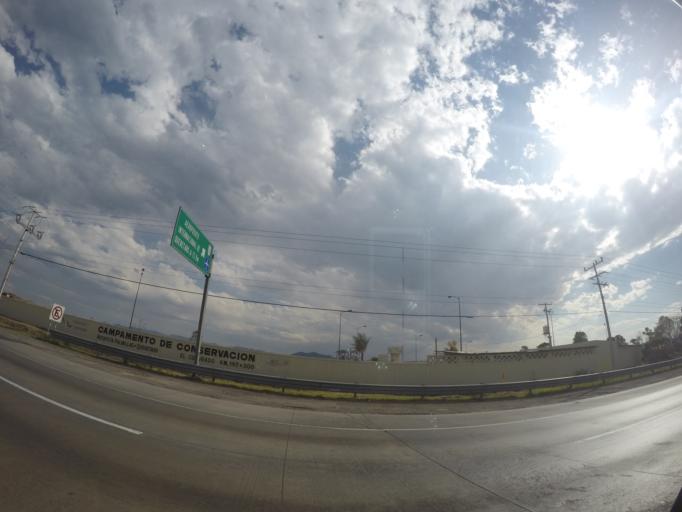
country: MX
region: Queretaro
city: Pedro Escobedo
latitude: 20.4955
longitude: -100.1311
